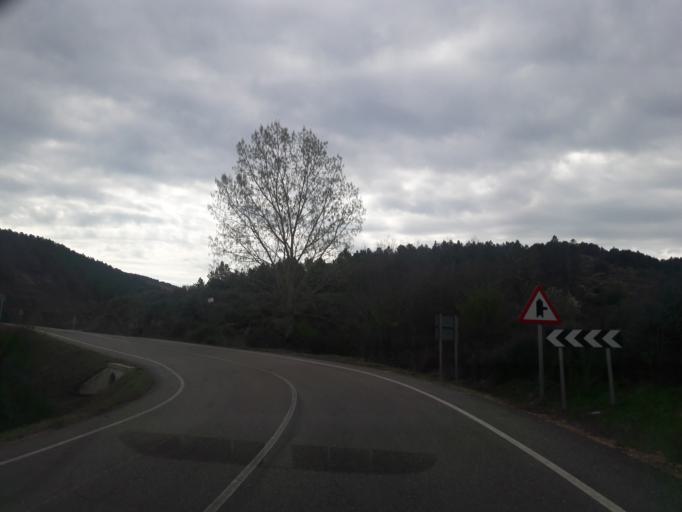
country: ES
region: Castille and Leon
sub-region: Provincia de Salamanca
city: Serradilla del Arroyo
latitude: 40.5154
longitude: -6.3919
